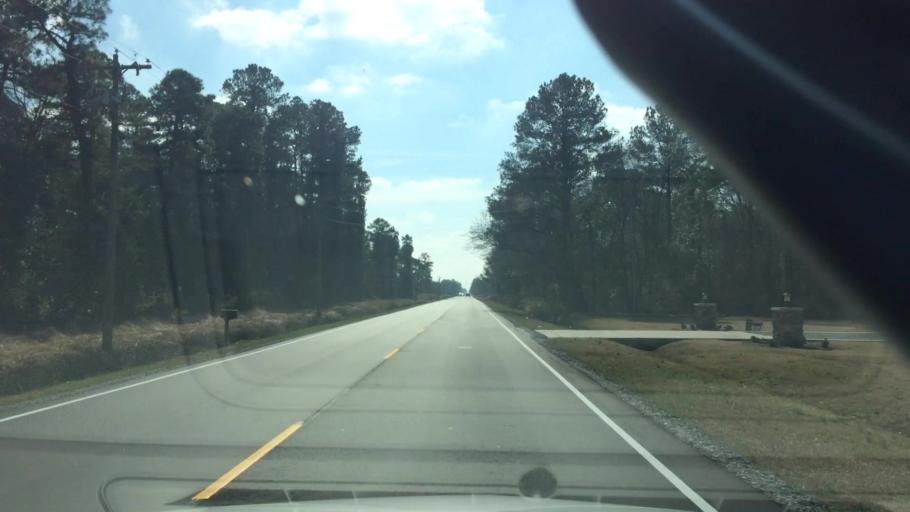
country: US
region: North Carolina
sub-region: Duplin County
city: Beulaville
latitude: 35.0253
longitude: -77.7492
